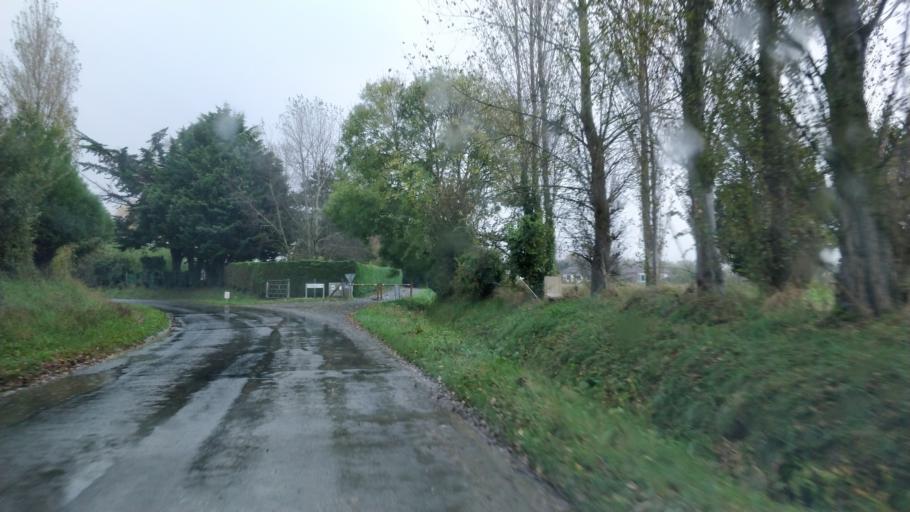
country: FR
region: Lower Normandy
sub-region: Departement de la Manche
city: Brehal
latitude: 48.9018
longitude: -1.5454
